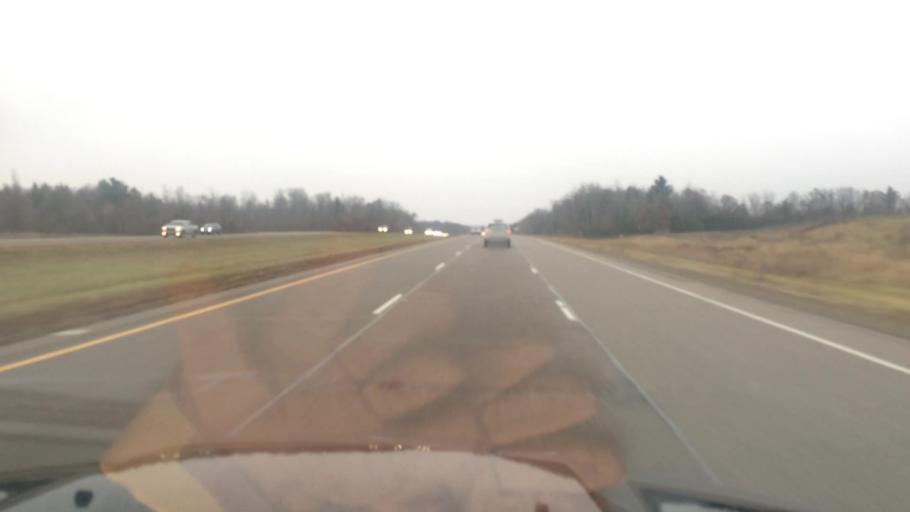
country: US
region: Wisconsin
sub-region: Portage County
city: Stevens Point
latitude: 44.5946
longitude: -89.6137
